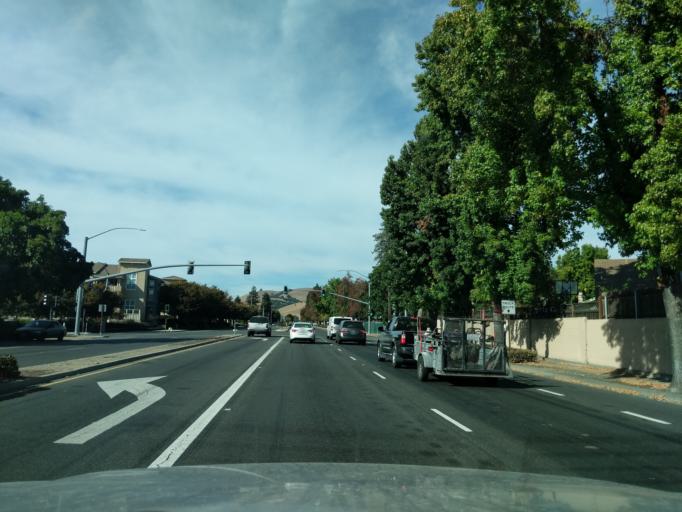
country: US
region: California
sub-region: Alameda County
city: Fremont
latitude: 37.5650
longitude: -121.9611
